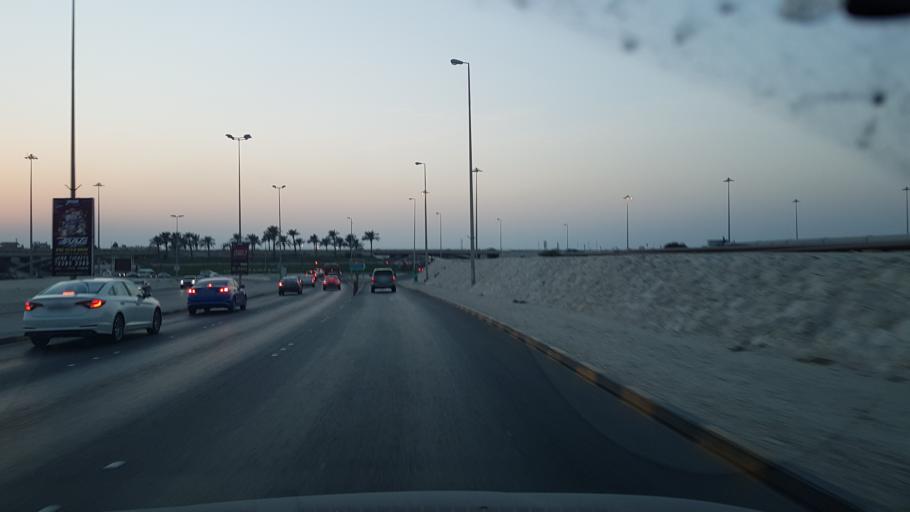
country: BH
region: Central Governorate
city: Madinat Hamad
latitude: 26.1396
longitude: 50.5134
